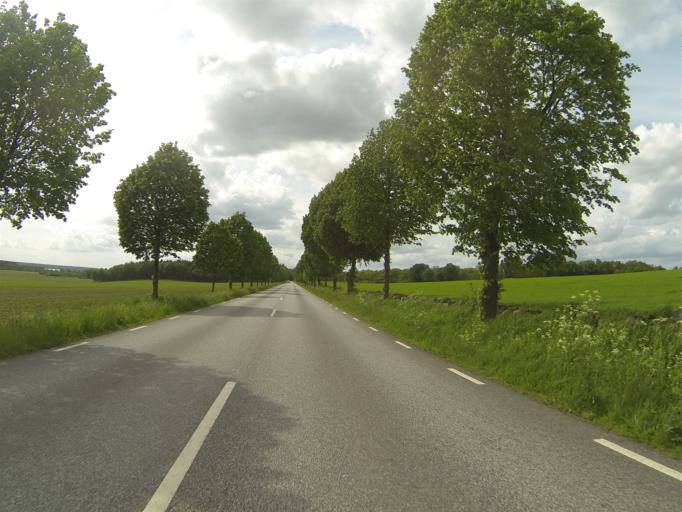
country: SE
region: Skane
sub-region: Sjobo Kommun
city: Sjoebo
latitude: 55.6802
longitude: 13.6483
